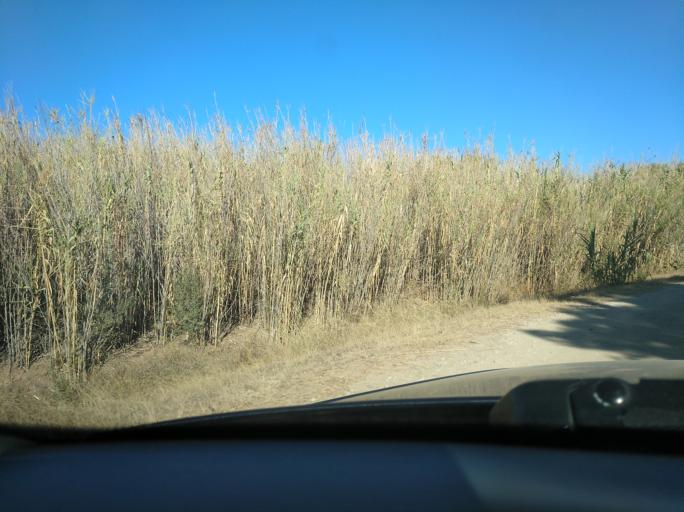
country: PT
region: Faro
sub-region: Vila Real de Santo Antonio
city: Monte Gordo
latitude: 37.1709
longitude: -7.5070
